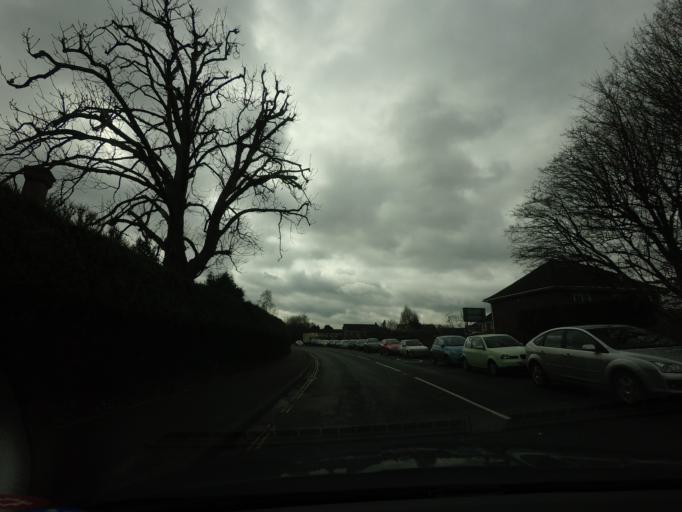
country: GB
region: England
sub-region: Kent
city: Shoreham
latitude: 51.3116
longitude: 0.1897
